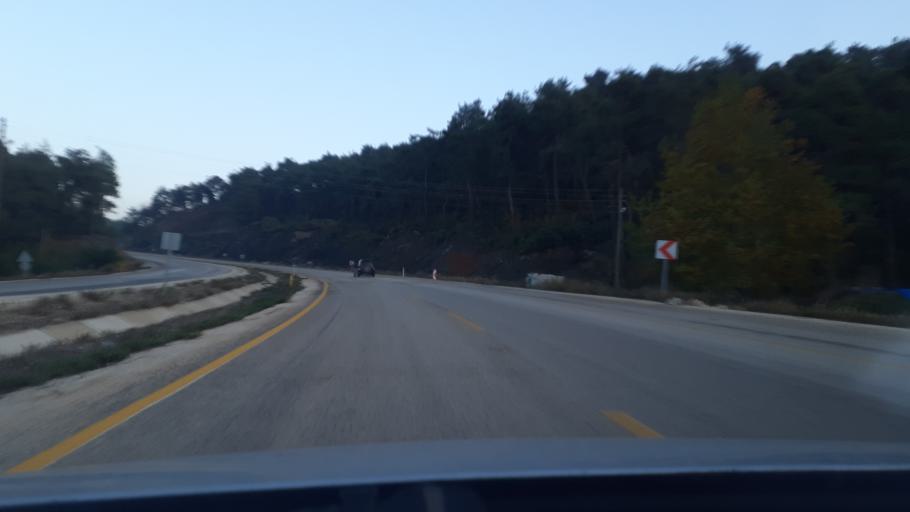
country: TR
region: Hatay
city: Yayladagi
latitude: 35.8912
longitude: 36.0869
